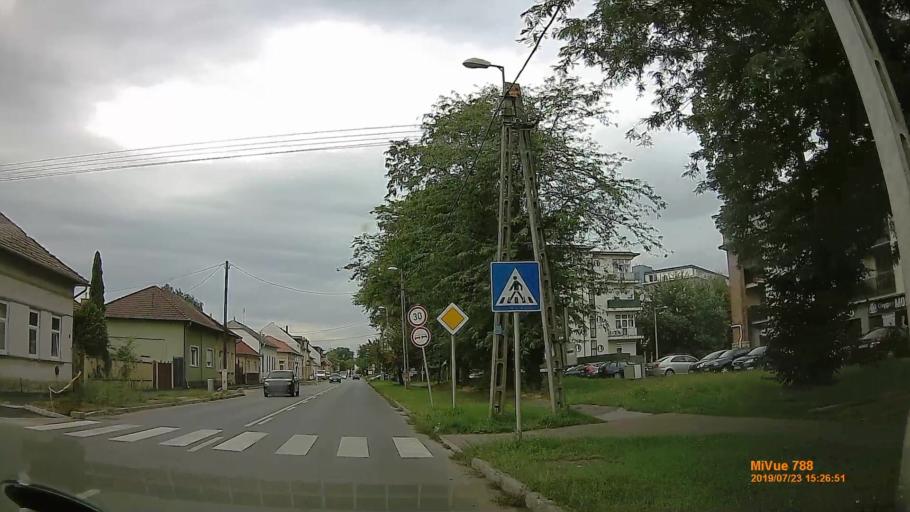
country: HU
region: Szabolcs-Szatmar-Bereg
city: Nyiregyhaza
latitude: 47.9466
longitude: 21.7337
